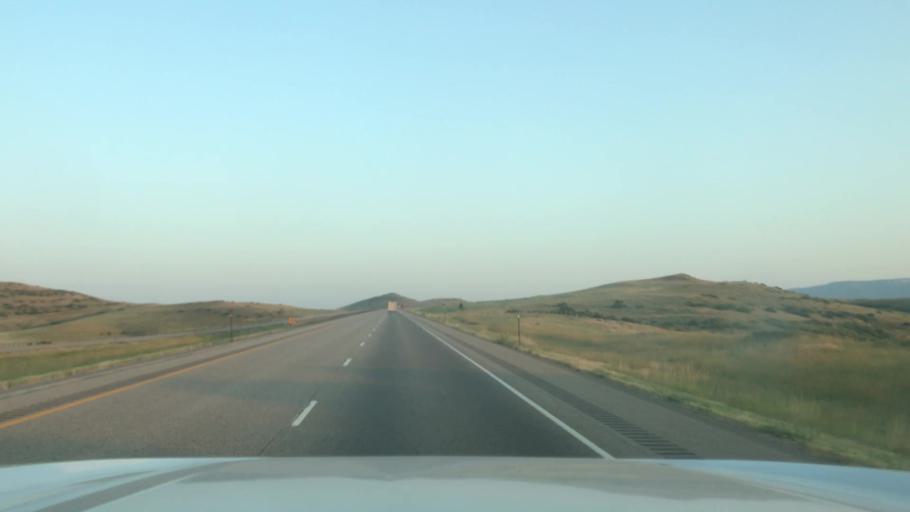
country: US
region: Wyoming
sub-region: Sheridan County
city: Sheridan
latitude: 44.7175
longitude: -106.9153
